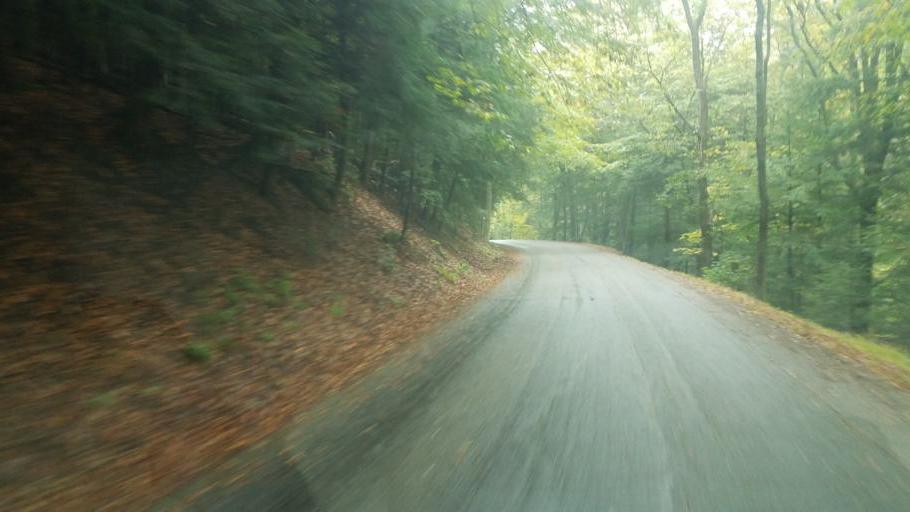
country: US
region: Ohio
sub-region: Ashland County
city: Loudonville
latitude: 40.6162
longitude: -82.3140
